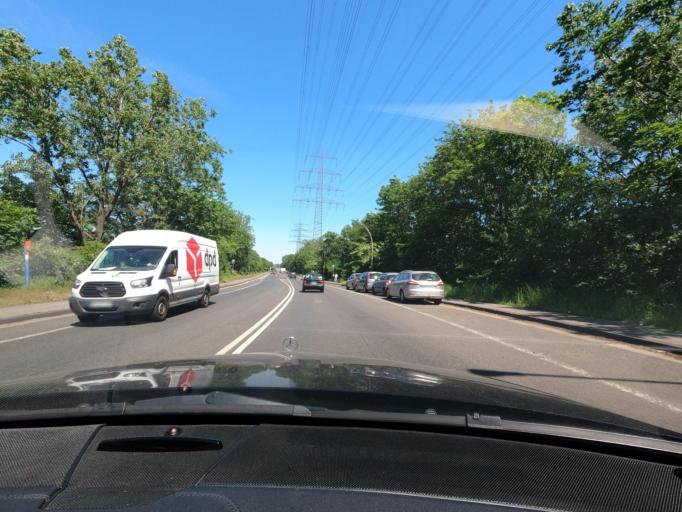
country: DE
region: North Rhine-Westphalia
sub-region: Regierungsbezirk Dusseldorf
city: Hochfeld
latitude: 51.3623
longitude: 6.7106
